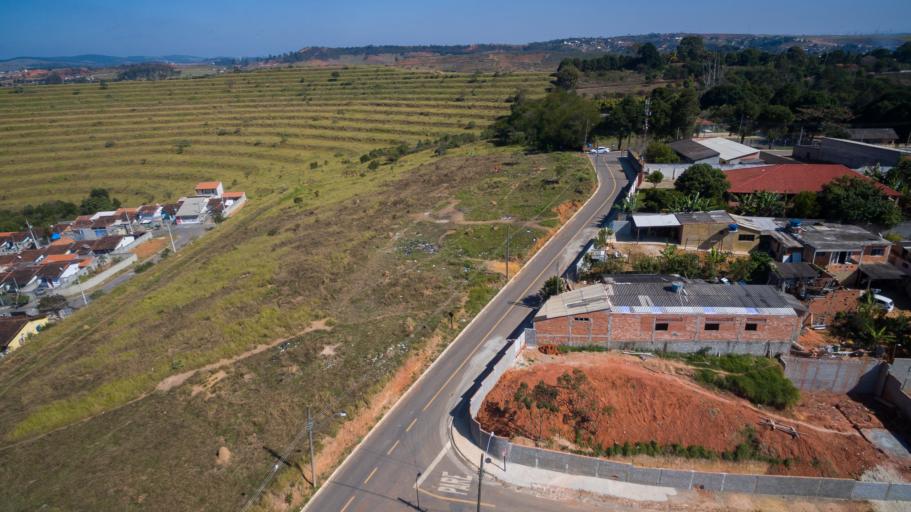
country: BR
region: Sao Paulo
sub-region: Sao Jose Dos Campos
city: Sao Jose dos Campos
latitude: -23.2247
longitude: -45.7959
